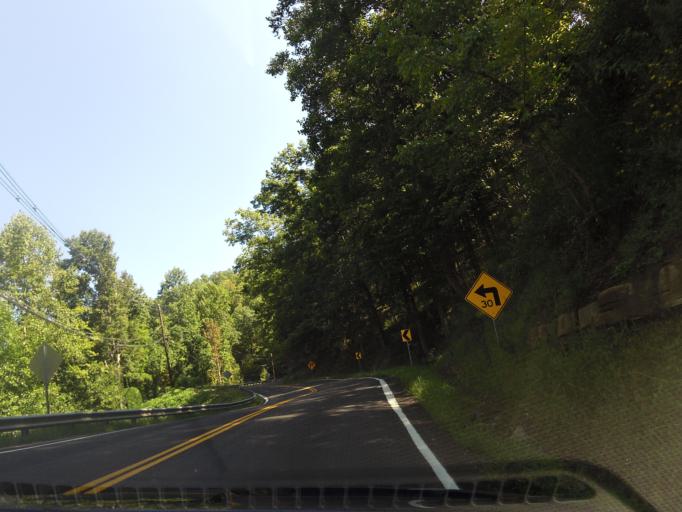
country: US
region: Kentucky
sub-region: Clay County
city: Manchester
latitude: 37.0988
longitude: -83.6678
